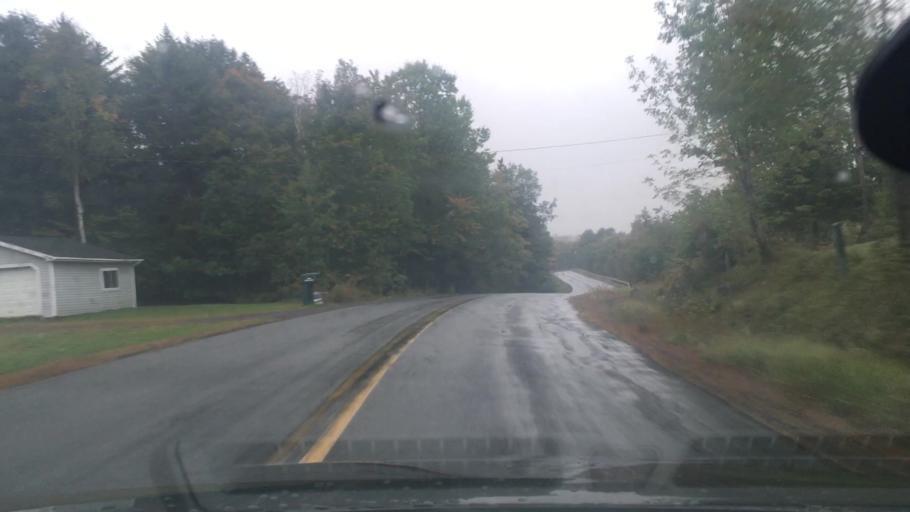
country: CA
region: Nova Scotia
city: Windsor
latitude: 44.8337
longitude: -64.2565
